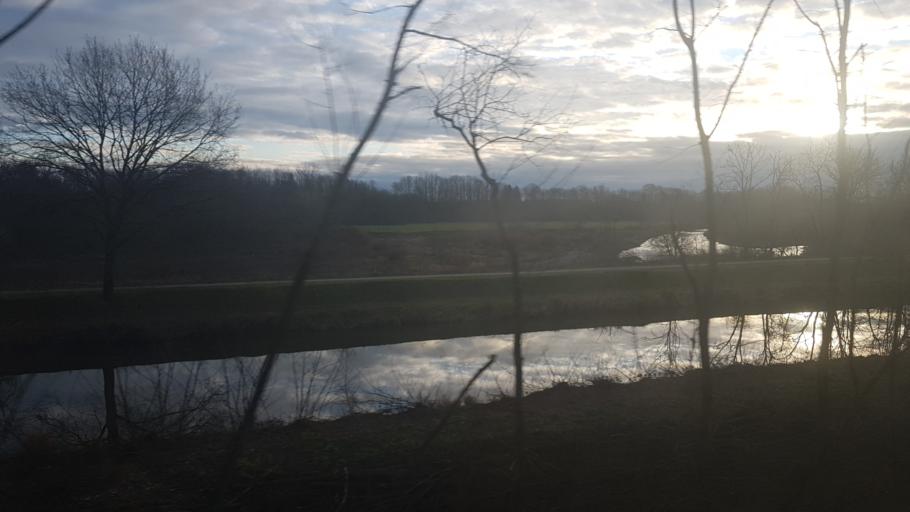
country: FR
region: Lorraine
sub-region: Departement des Vosges
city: Igney
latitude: 48.2881
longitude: 6.3975
